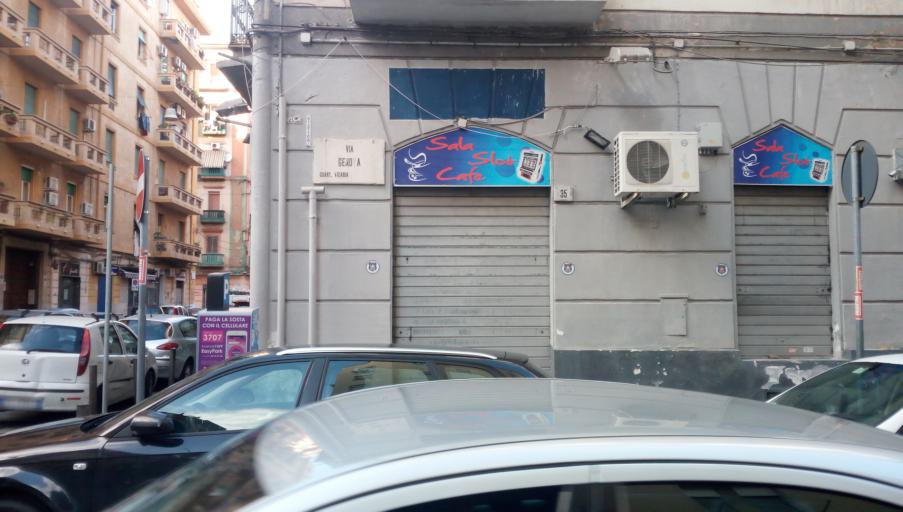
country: IT
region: Campania
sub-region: Provincia di Napoli
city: Napoli
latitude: 40.8552
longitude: 14.2734
